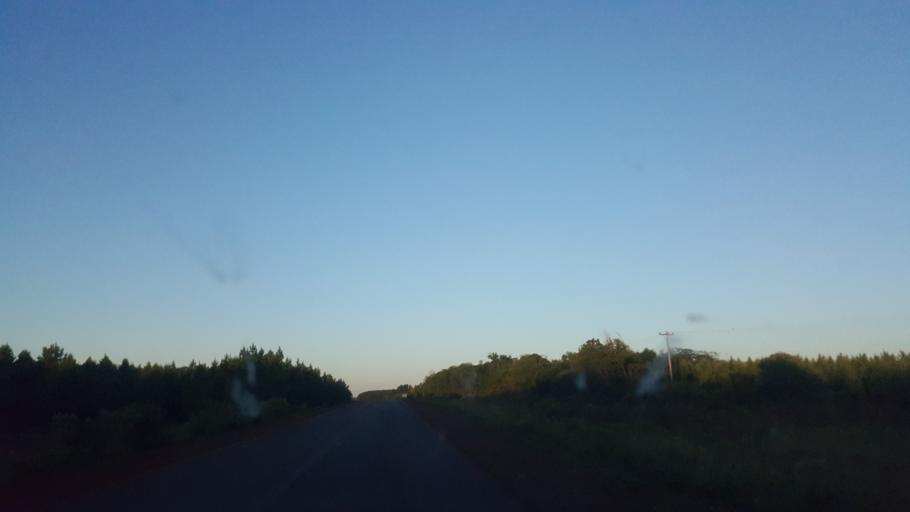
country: AR
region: Corrientes
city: Santo Tome
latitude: -28.4327
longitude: -55.9971
